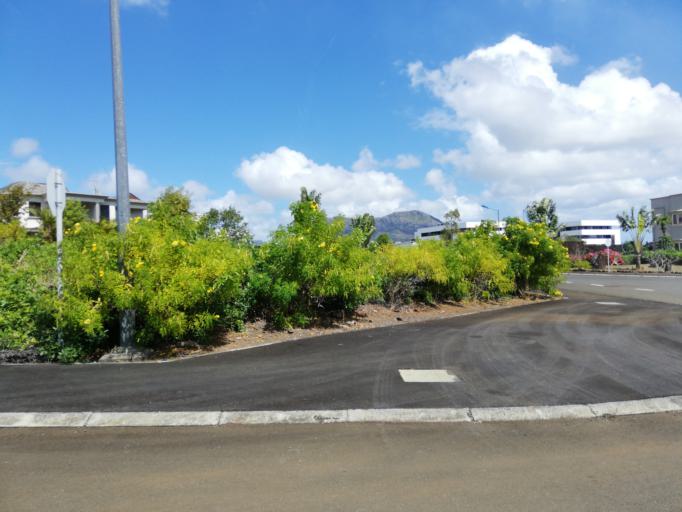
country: MU
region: Plaines Wilhems
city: Ebene
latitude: -20.2391
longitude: 57.4868
